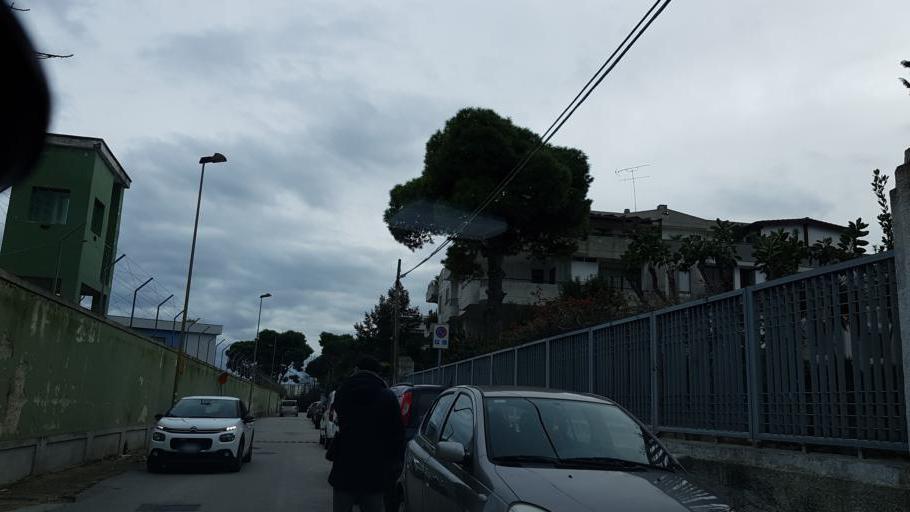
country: IT
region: Apulia
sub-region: Provincia di Brindisi
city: Materdomini
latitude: 40.6479
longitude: 17.9482
